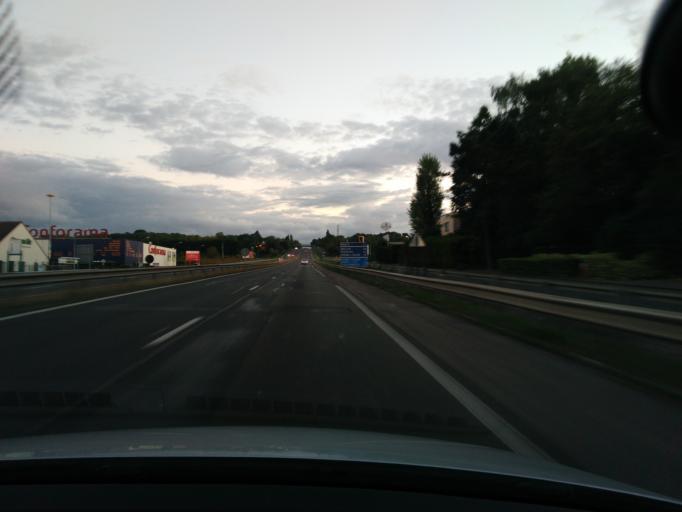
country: FR
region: Ile-de-France
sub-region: Departement de Seine-et-Marne
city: Nanteuil-les-Meaux
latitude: 48.9363
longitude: 2.8798
